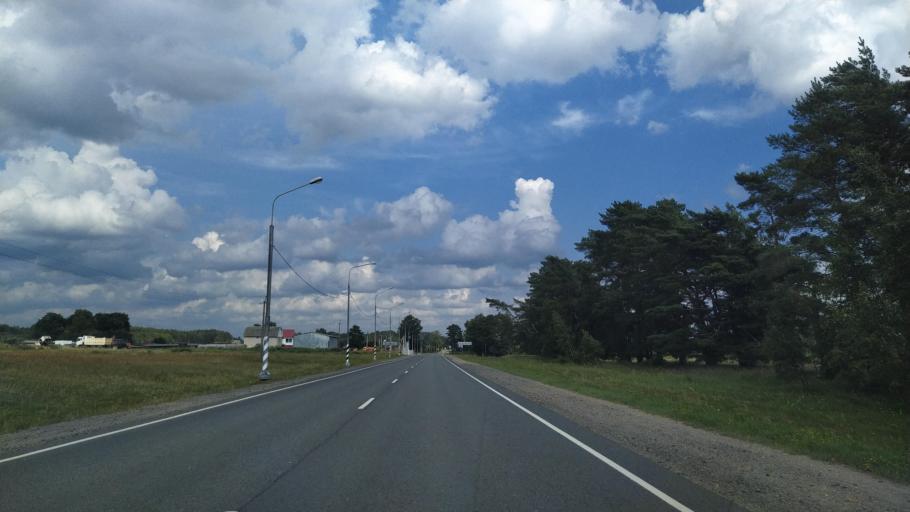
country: RU
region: Novgorod
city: Sol'tsy
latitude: 58.1002
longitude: 30.1933
